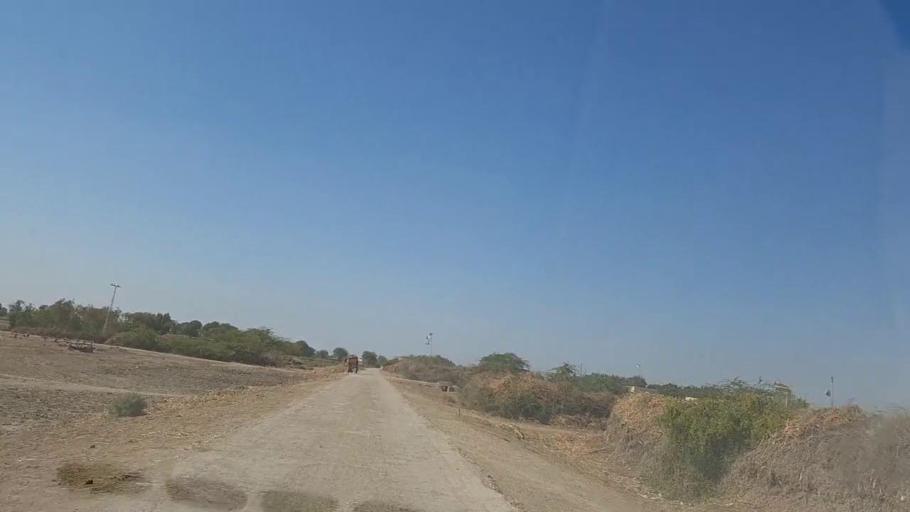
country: PK
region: Sindh
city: Digri
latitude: 25.1238
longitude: 69.0746
